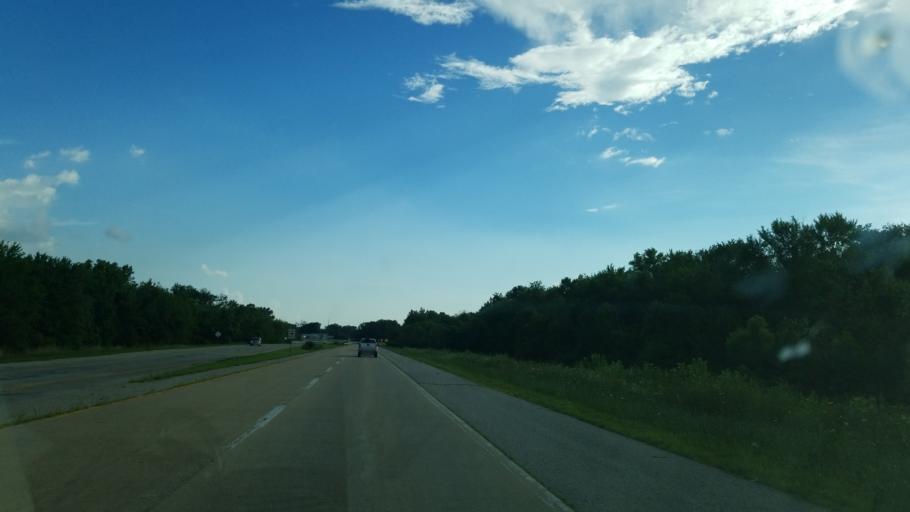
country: US
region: Illinois
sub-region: Marion County
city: Central City
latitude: 38.5587
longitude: -89.1244
